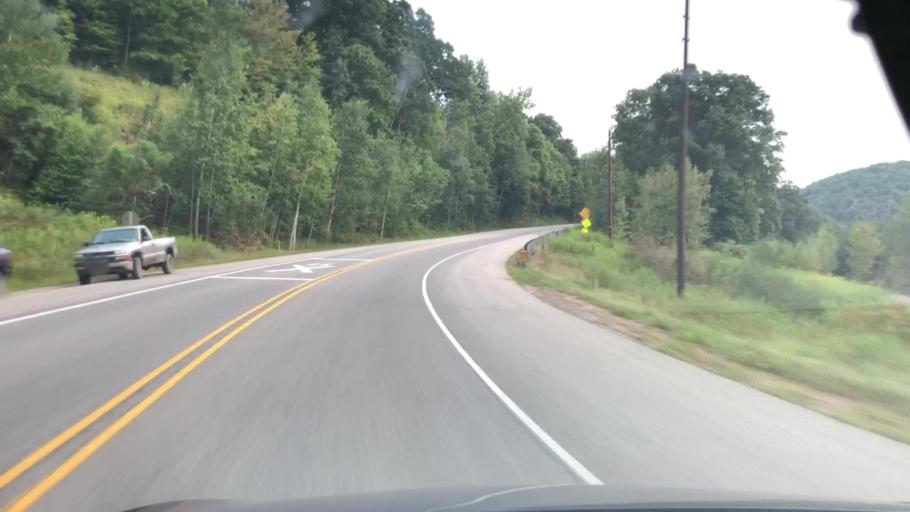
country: US
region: Pennsylvania
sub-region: Venango County
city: Hasson Heights
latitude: 41.4773
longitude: -79.6918
